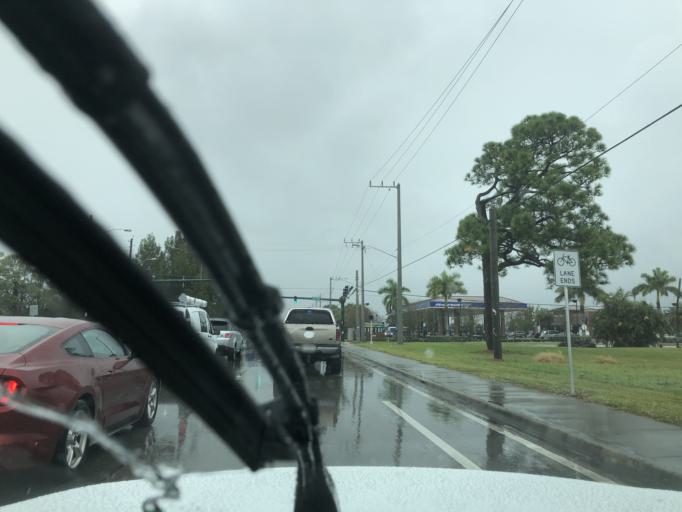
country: US
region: Florida
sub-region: Palm Beach County
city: Royal Palm Estates
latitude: 26.6803
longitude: -80.1202
